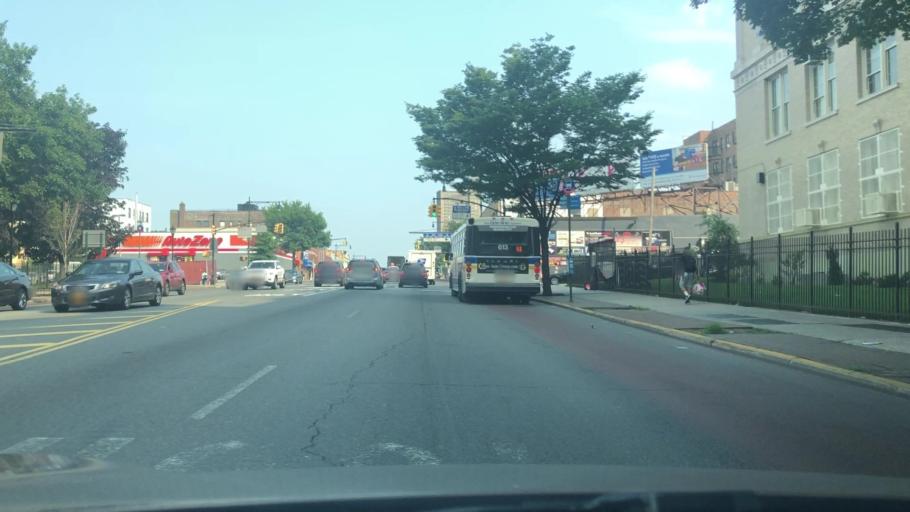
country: US
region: New York
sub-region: Bronx
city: The Bronx
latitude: 40.8599
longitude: -73.8881
